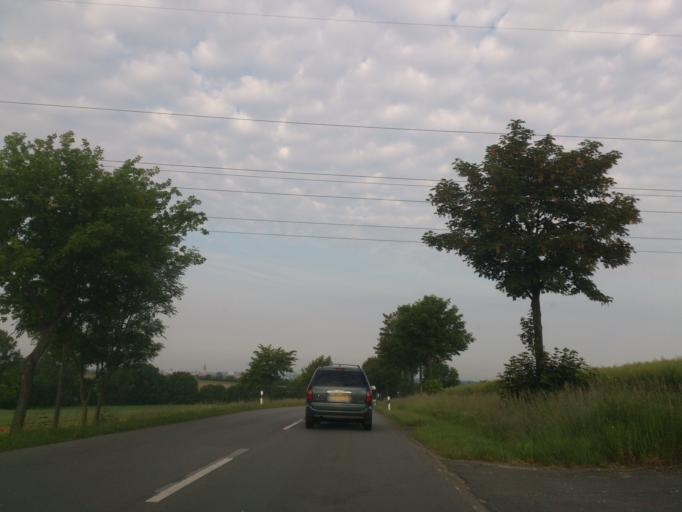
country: DE
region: North Rhine-Westphalia
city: Bad Lippspringe
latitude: 51.7337
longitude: 8.8051
